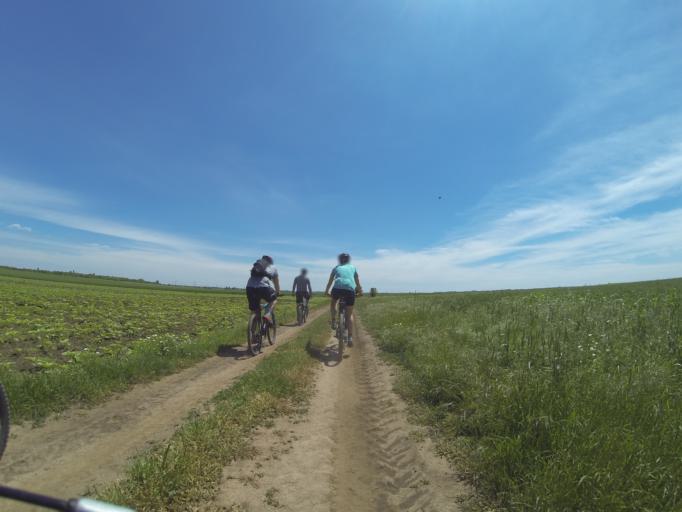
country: RO
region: Dolj
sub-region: Comuna Leu
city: Zanoaga
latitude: 44.1780
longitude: 24.0842
